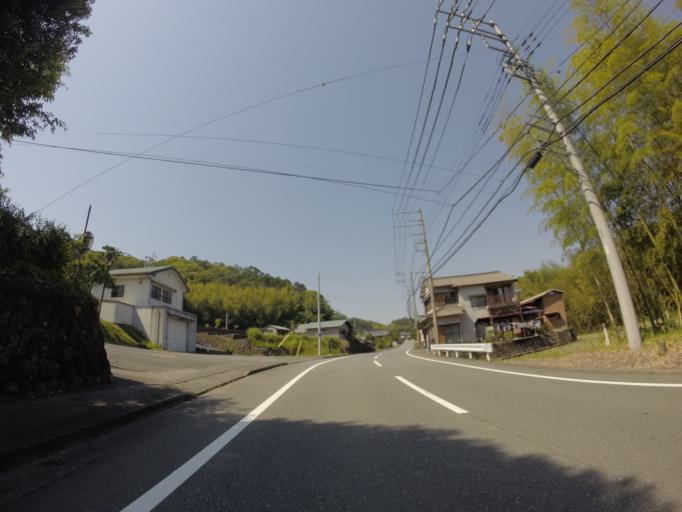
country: JP
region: Shizuoka
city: Fujinomiya
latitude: 35.2122
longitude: 138.5870
